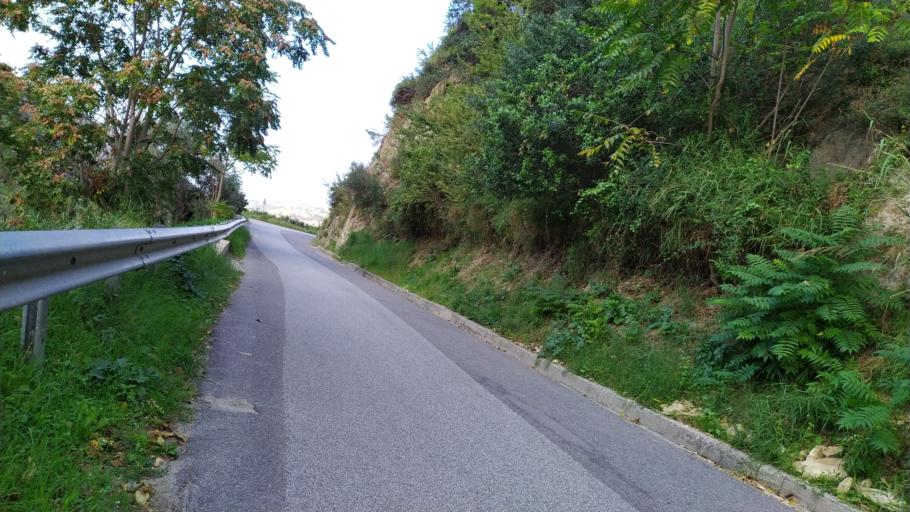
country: IT
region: Sicily
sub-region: Messina
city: Saponara
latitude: 38.1933
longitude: 15.4291
